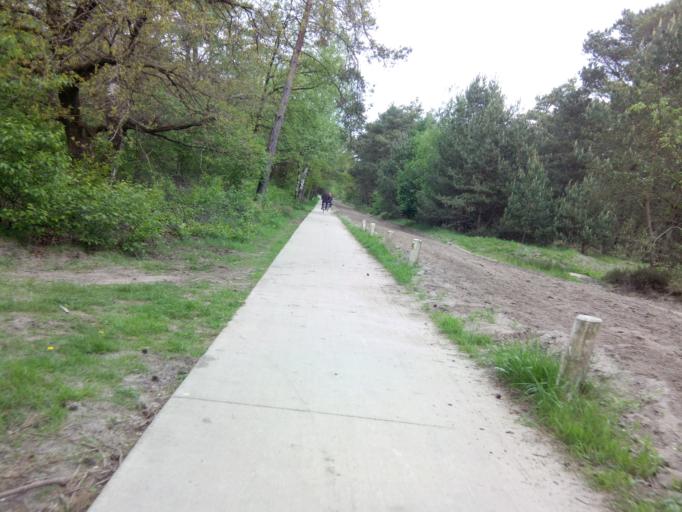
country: NL
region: Gelderland
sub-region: Gemeente Ede
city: Ede
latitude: 52.0610
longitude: 5.6963
